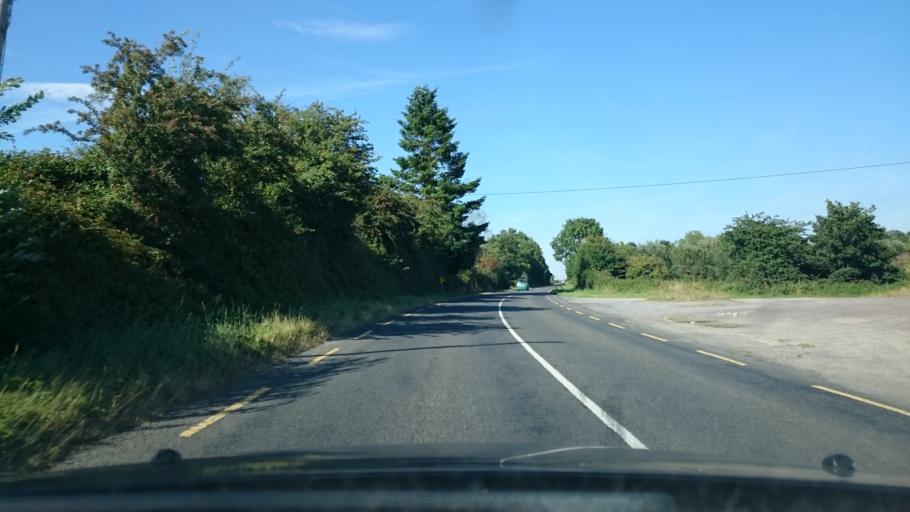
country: IE
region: Leinster
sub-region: Kilkenny
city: Graiguenamanagh
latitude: 52.5507
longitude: -6.9586
